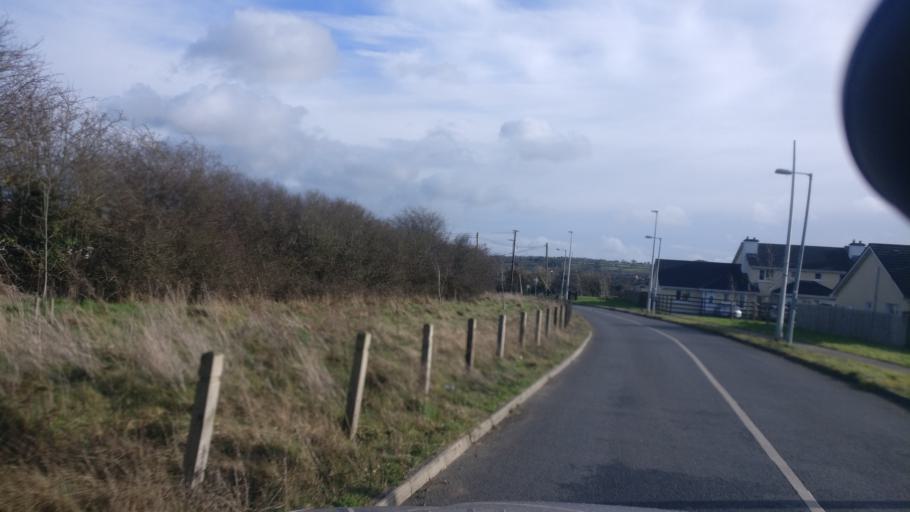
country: IE
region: Leinster
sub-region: Kilkenny
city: Thomastown
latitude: 52.5228
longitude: -7.1542
